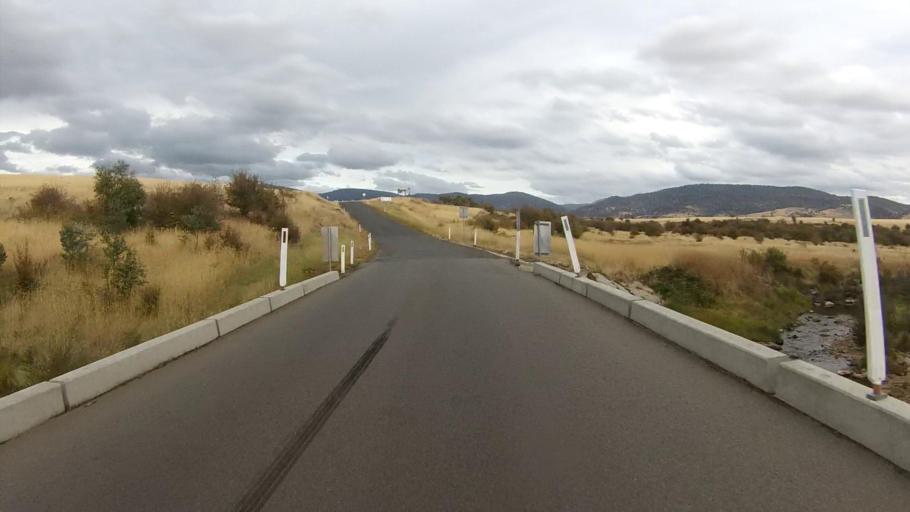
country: AU
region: Tasmania
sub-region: Northern Midlands
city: Evandale
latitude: -41.8169
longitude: 147.7538
